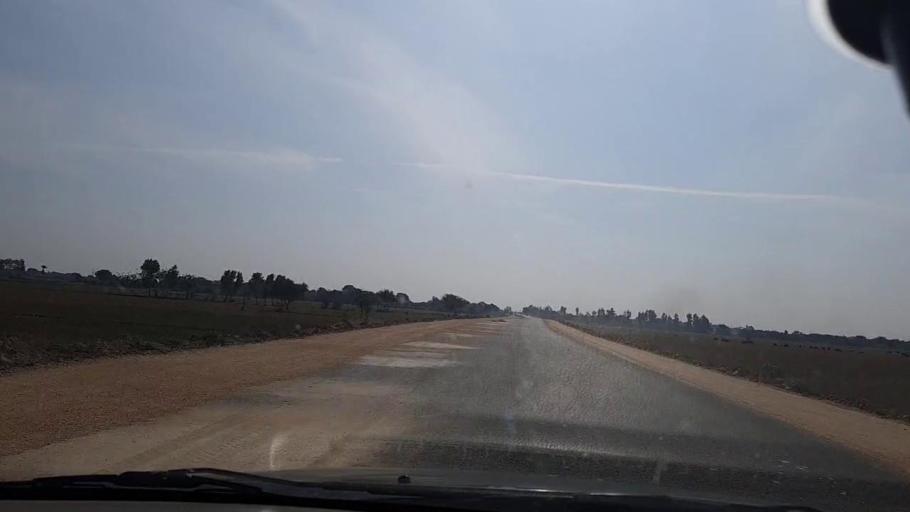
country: PK
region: Sindh
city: Mirpur Batoro
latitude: 24.7402
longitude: 68.2741
